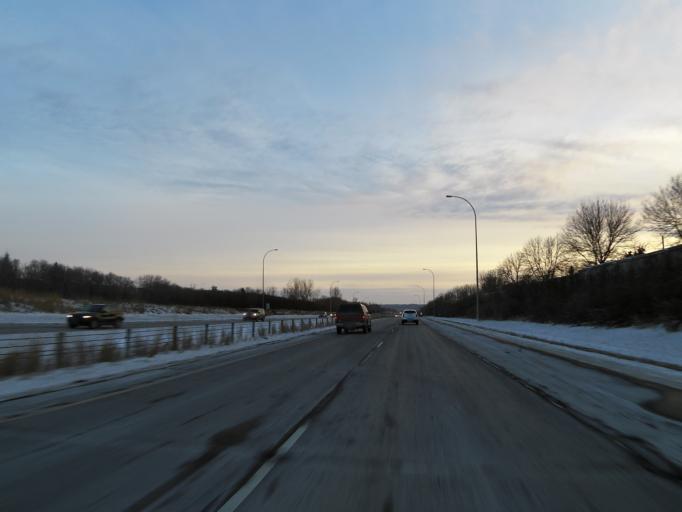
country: US
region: Minnesota
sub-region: Hennepin County
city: Eden Prairie
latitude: 44.8290
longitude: -93.3984
